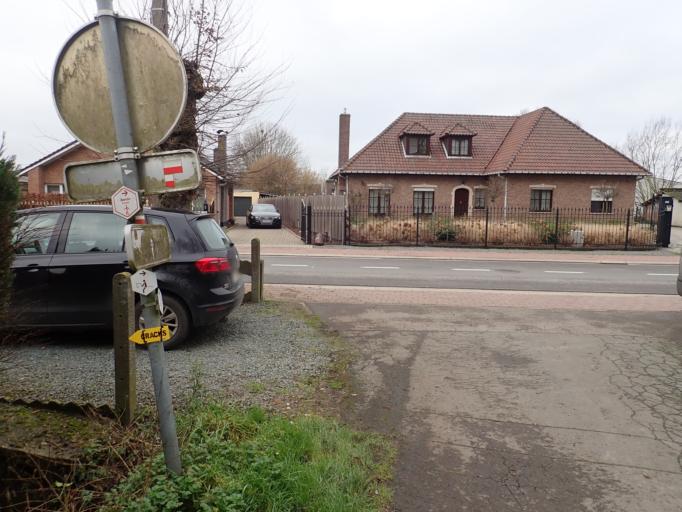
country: BE
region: Flanders
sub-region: Provincie Vlaams-Brabant
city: Londerzeel
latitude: 50.9672
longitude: 4.3006
